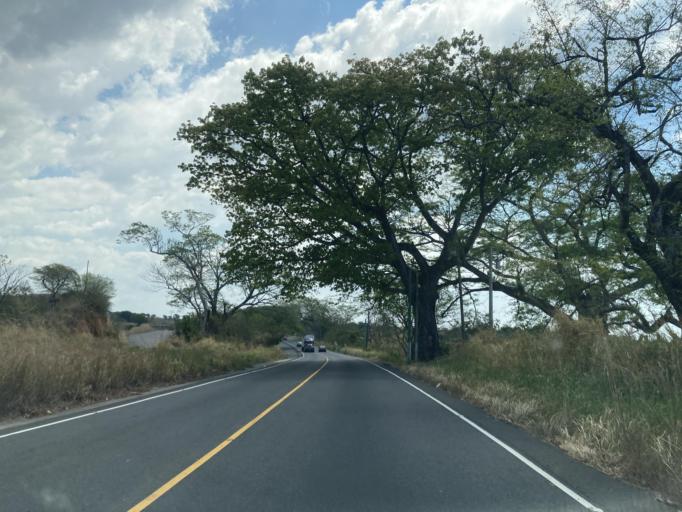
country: GT
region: Santa Rosa
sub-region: Municipio de Taxisco
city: Taxisco
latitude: 14.0948
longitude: -90.5269
